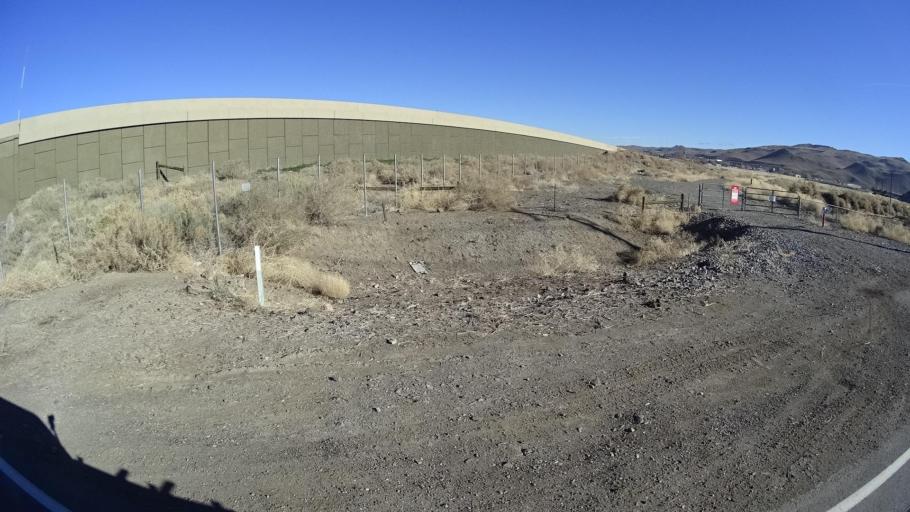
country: US
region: Nevada
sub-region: Washoe County
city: Sparks
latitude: 39.5129
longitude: -119.7128
